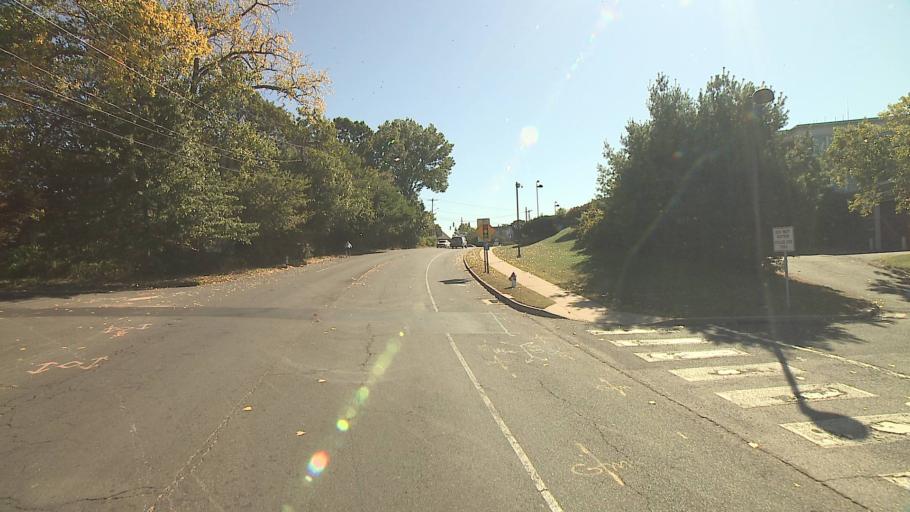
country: US
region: Connecticut
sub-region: New Haven County
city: West Haven
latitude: 41.2740
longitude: -72.9649
